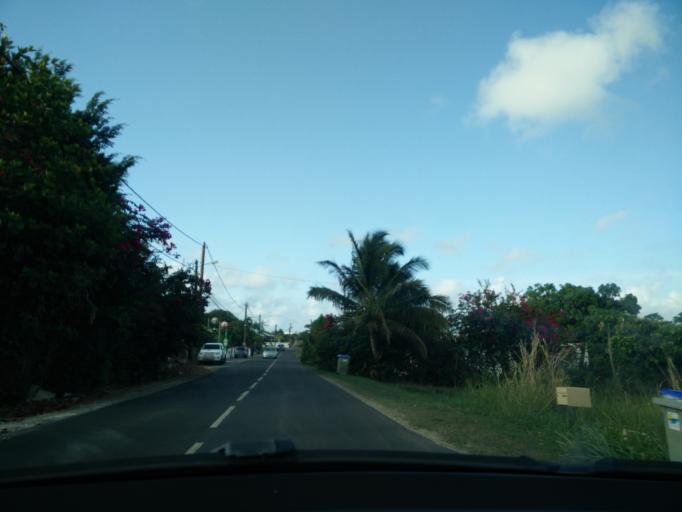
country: GP
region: Guadeloupe
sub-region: Guadeloupe
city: Le Moule
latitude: 16.2912
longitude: -61.3692
